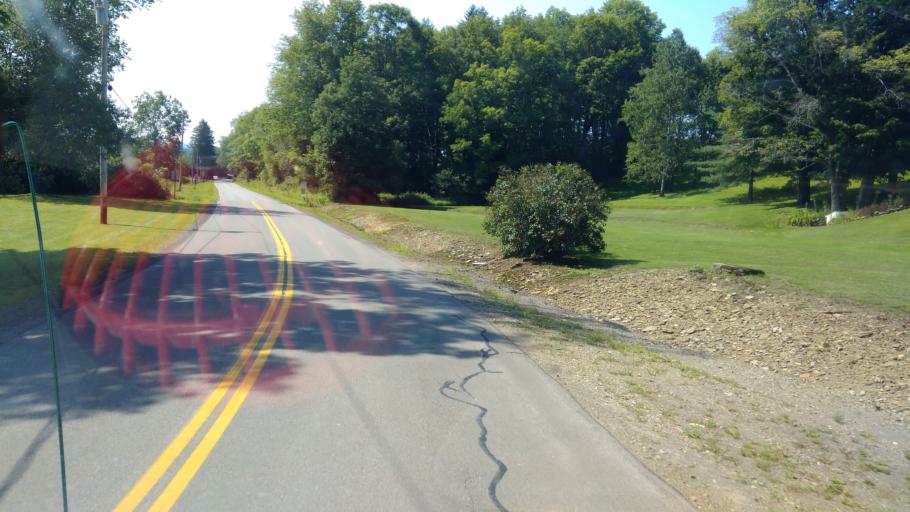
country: US
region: New York
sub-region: Allegany County
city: Belmont
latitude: 42.2604
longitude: -78.0006
